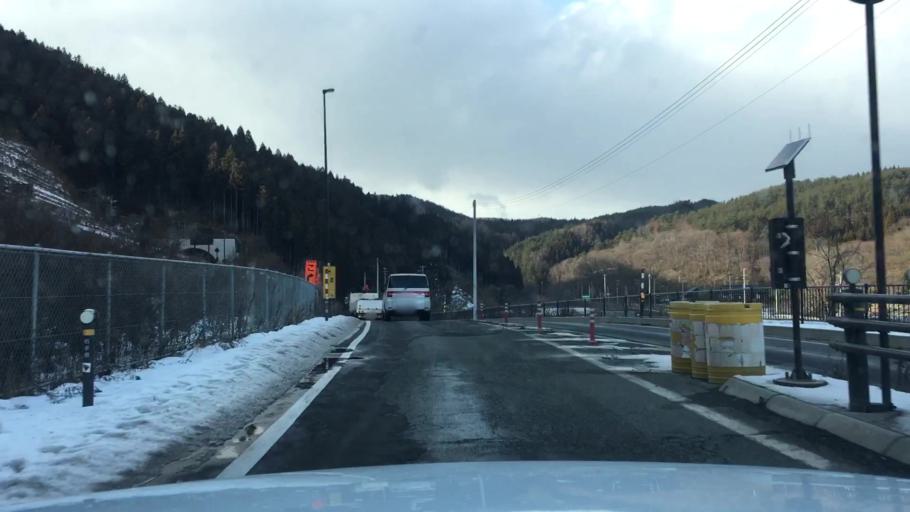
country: JP
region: Iwate
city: Morioka-shi
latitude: 39.6718
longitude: 141.2306
